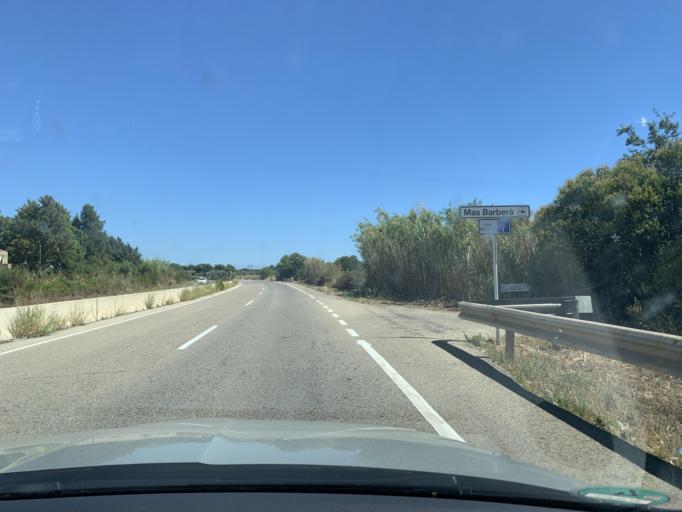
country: ES
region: Catalonia
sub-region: Provincia de Tarragona
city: Vila-seca
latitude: 41.1360
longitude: 1.1363
